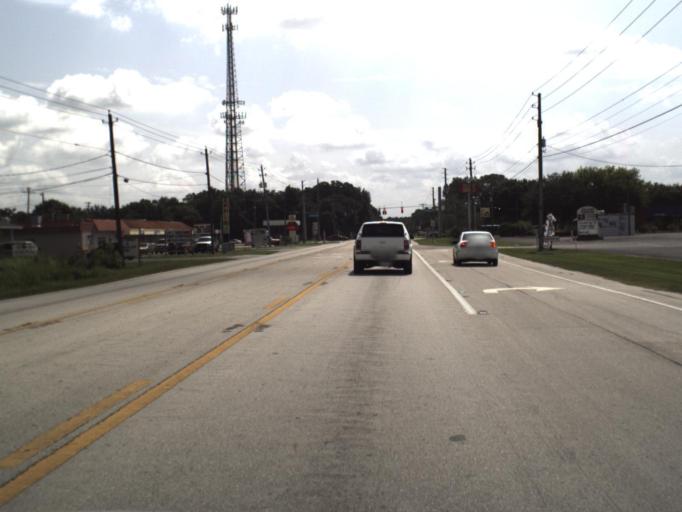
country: US
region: Florida
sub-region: Polk County
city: Jan-Phyl Village
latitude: 28.0177
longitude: -81.7617
